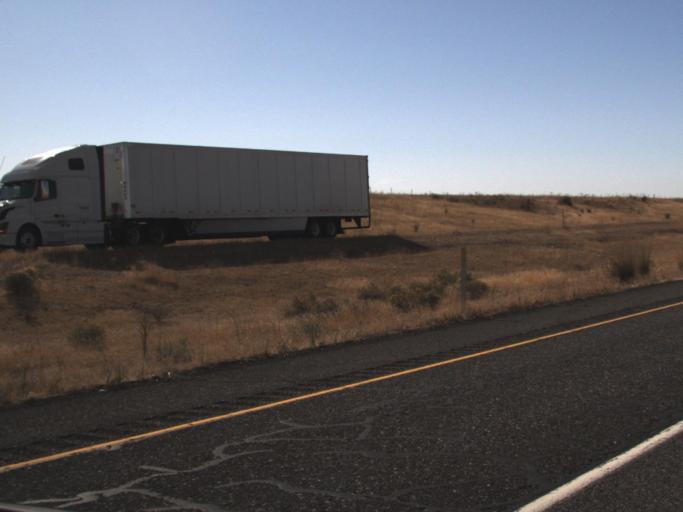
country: US
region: Washington
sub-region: Franklin County
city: Basin City
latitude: 46.5383
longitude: -119.0127
